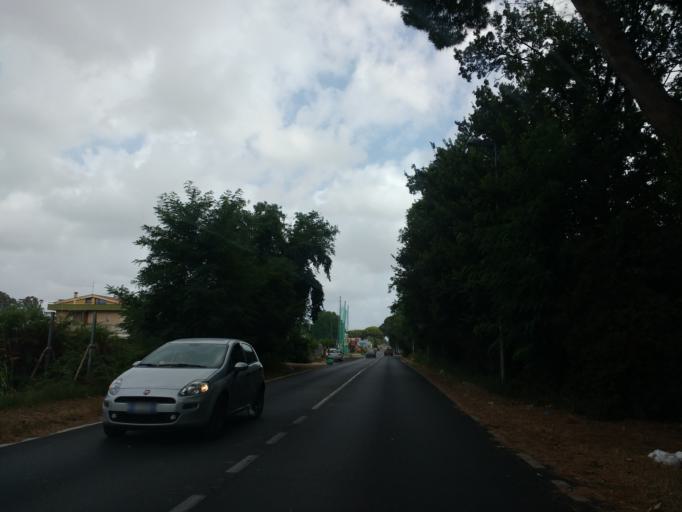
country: IT
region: Latium
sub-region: Citta metropolitana di Roma Capitale
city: Lavinio
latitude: 41.4925
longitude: 12.5948
